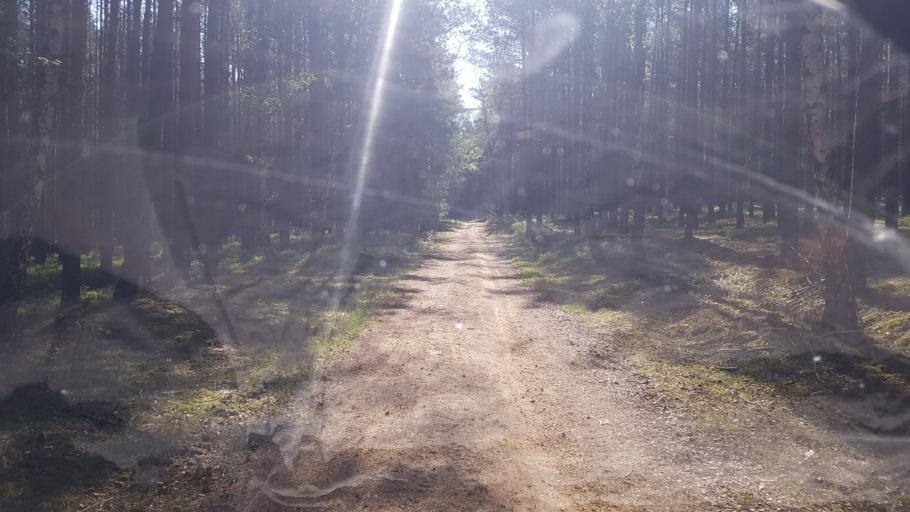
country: DE
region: Brandenburg
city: Crinitz
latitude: 51.7368
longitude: 13.7751
